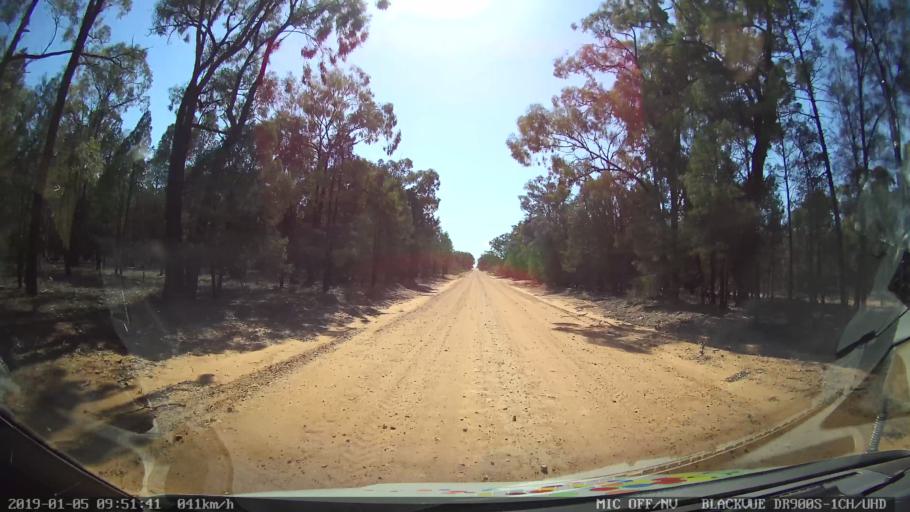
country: AU
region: New South Wales
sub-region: Gilgandra
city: Gilgandra
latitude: -31.6609
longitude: 148.7619
